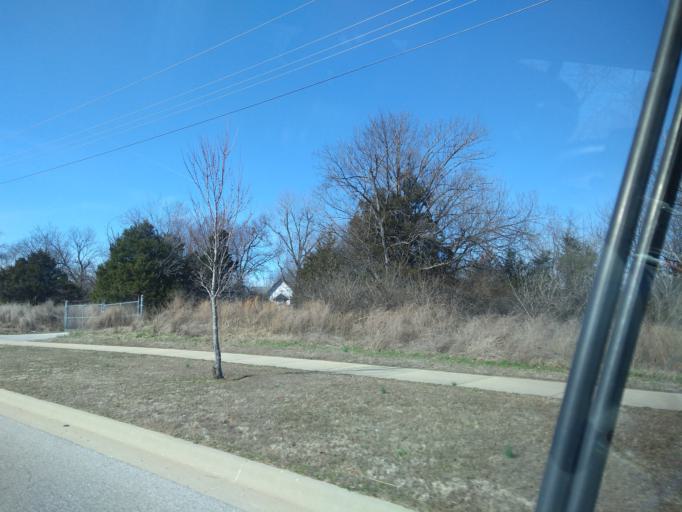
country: US
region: Arkansas
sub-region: Washington County
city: Farmington
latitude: 36.0591
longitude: -94.2350
